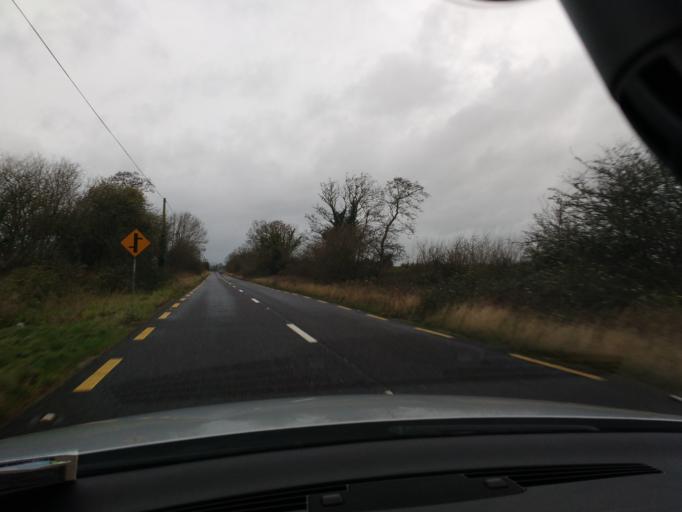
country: IE
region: Munster
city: Thurles
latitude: 52.6718
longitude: -7.7363
